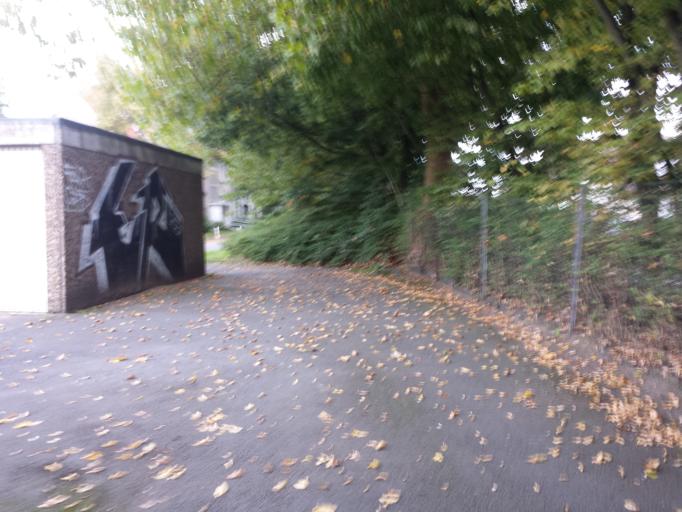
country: DE
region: North Rhine-Westphalia
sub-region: Regierungsbezirk Detmold
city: Guetersloh
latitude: 51.9115
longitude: 8.3637
